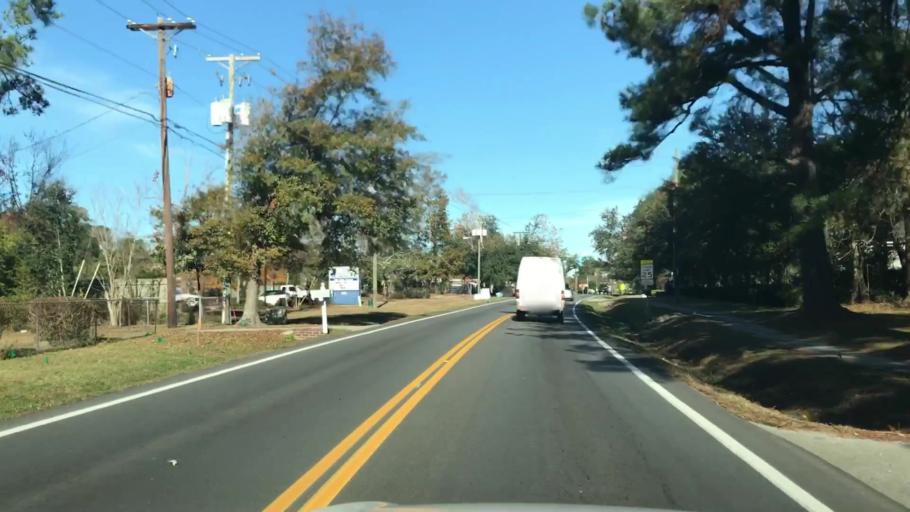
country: US
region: South Carolina
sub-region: Dorchester County
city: Summerville
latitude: 33.0066
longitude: -80.2357
